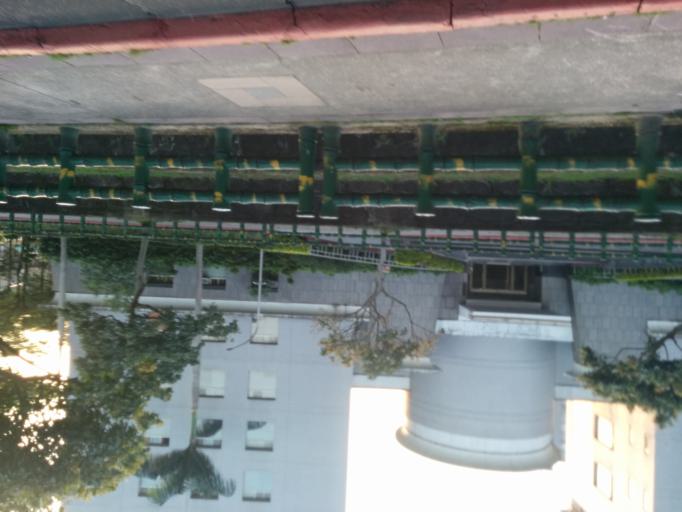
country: TW
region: Taipei
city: Taipei
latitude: 25.0423
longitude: 121.6127
